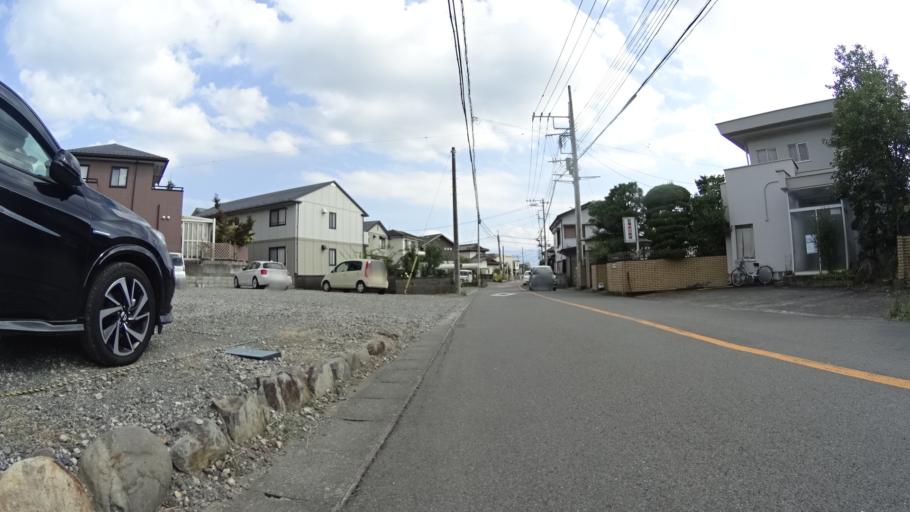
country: JP
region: Yamanashi
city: Kofu-shi
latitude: 35.6846
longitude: 138.5663
